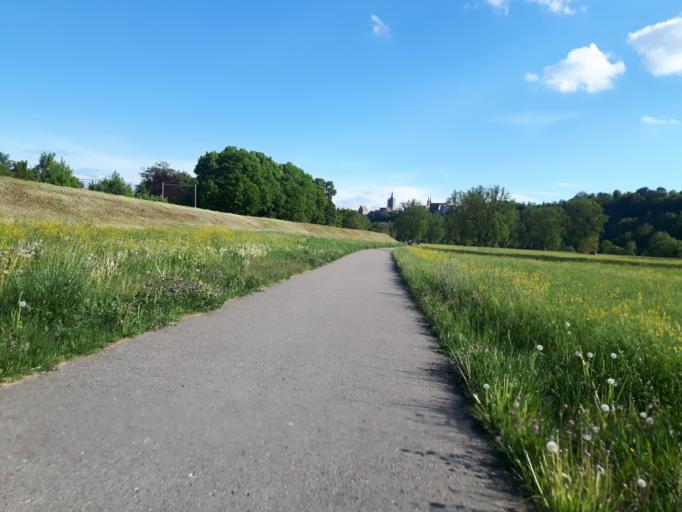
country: DE
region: Baden-Wuerttemberg
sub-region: Regierungsbezirk Stuttgart
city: Offenau
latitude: 49.2411
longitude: 9.1598
